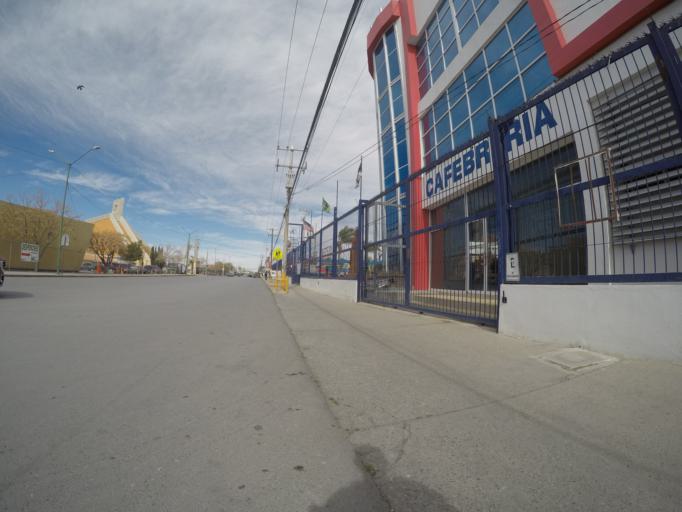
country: MX
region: Chihuahua
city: Ciudad Juarez
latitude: 31.7194
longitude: -106.4317
